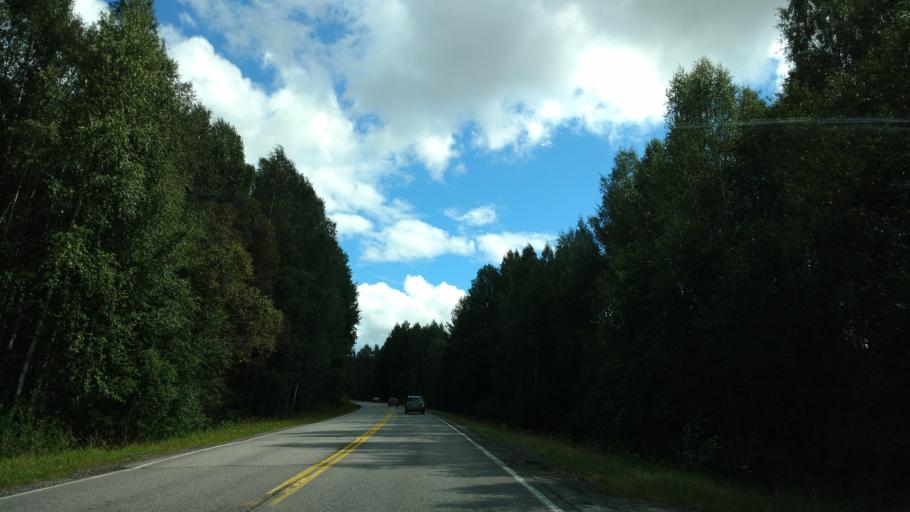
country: FI
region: Uusimaa
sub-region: Helsinki
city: Karjalohja
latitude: 60.2121
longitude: 23.6490
